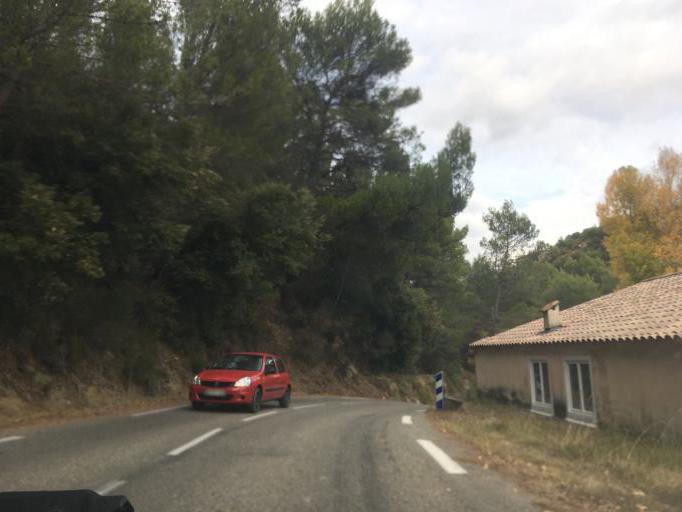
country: FR
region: Provence-Alpes-Cote d'Azur
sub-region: Departement du Var
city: Villecroze
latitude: 43.5923
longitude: 6.2799
